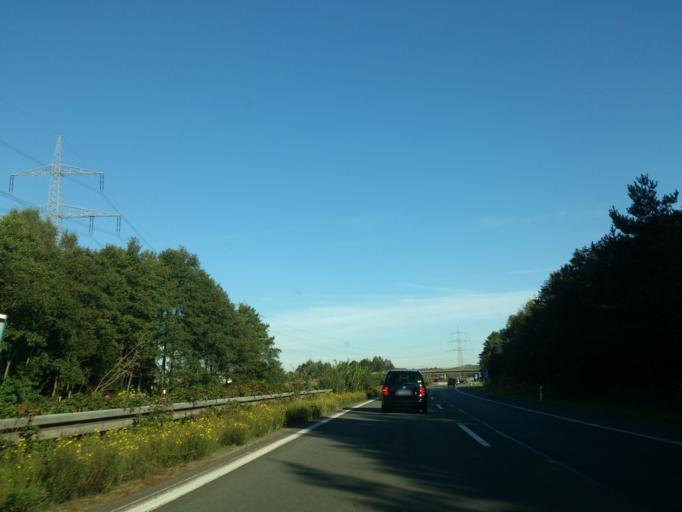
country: DE
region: North Rhine-Westphalia
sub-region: Regierungsbezirk Detmold
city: Oerlinghausen
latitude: 51.9123
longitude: 8.6193
